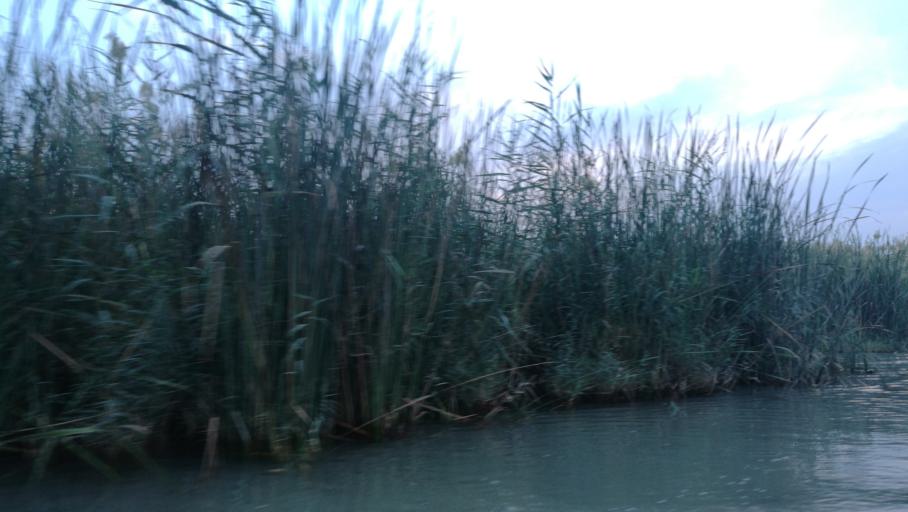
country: IQ
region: Dhi Qar
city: Al Jabayish
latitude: 30.9860
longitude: 47.0410
